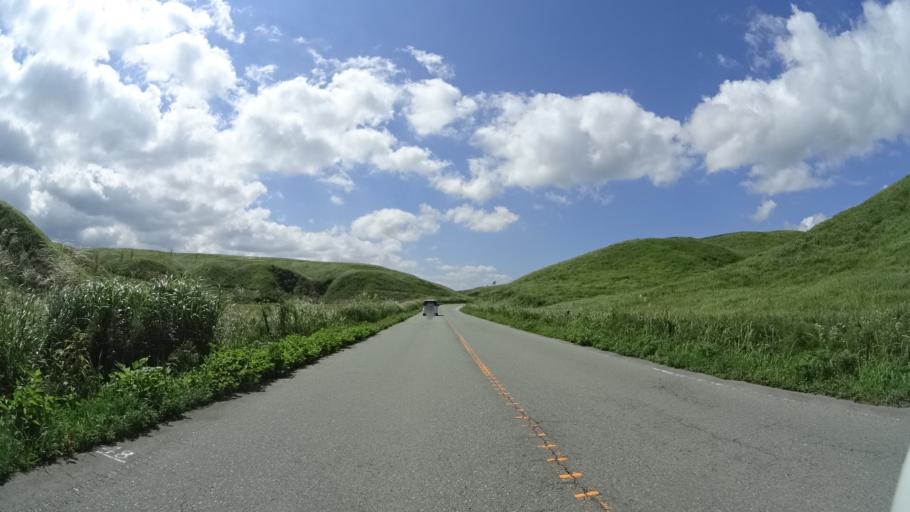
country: JP
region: Kumamoto
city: Aso
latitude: 33.0081
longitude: 131.1453
